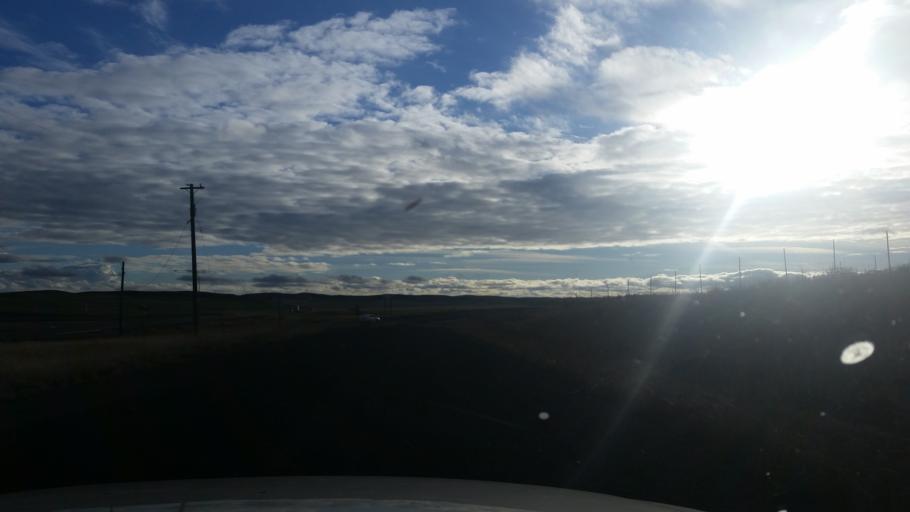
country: US
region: Washington
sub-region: Spokane County
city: Cheney
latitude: 47.4259
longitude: -117.3901
